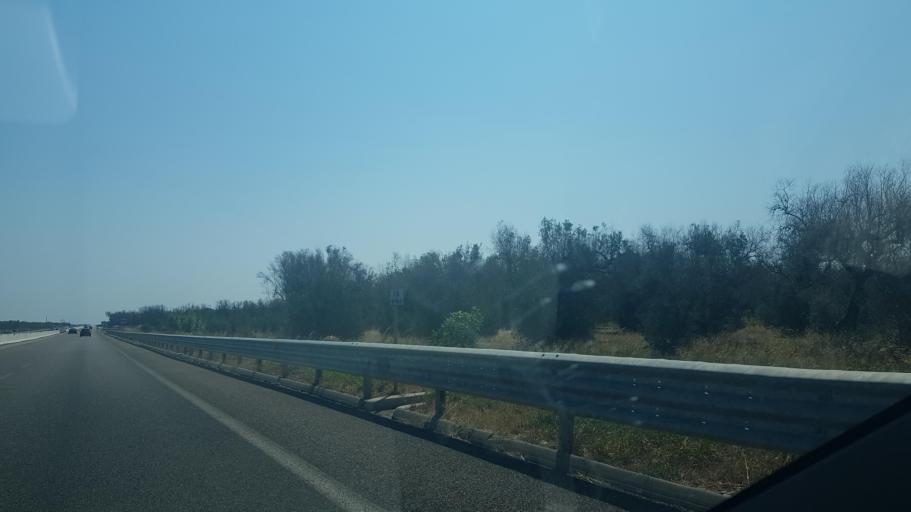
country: IT
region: Apulia
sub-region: Provincia di Lecce
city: Giurdignano
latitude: 40.1390
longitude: 18.4248
